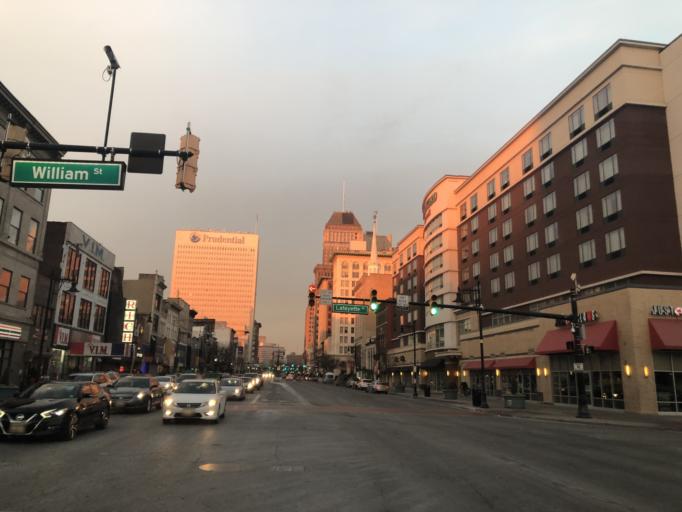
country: US
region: New Jersey
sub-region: Essex County
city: Newark
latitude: 40.7331
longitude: -74.1735
